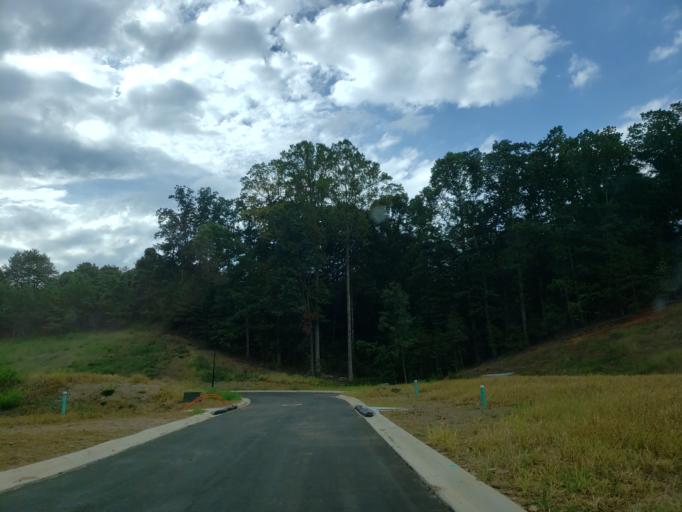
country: US
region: Georgia
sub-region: Pickens County
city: Jasper
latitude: 34.4458
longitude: -84.4514
